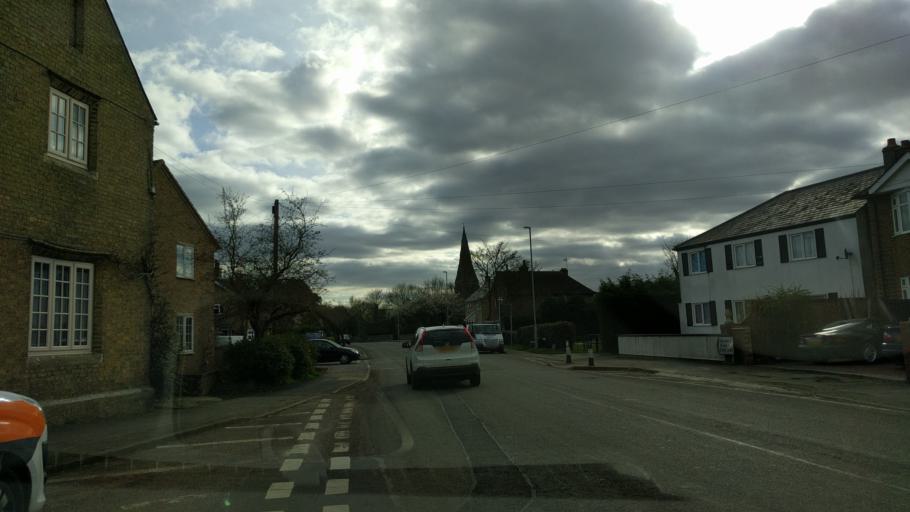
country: GB
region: England
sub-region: Cambridgeshire
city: Warboys
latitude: 52.4030
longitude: -0.0853
